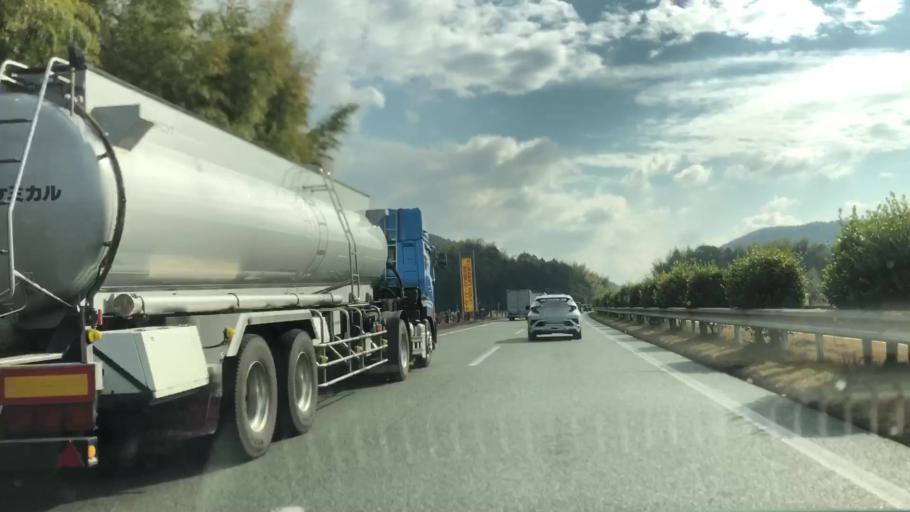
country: JP
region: Fukuoka
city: Setakamachi-takayanagi
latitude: 33.1081
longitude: 130.5333
